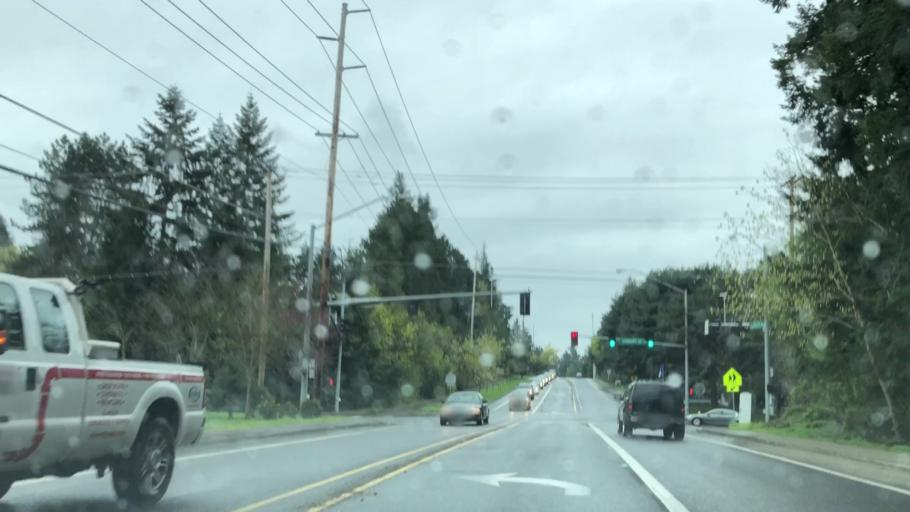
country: US
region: Oregon
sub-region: Washington County
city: Raleigh Hills
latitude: 45.4770
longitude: -122.7472
